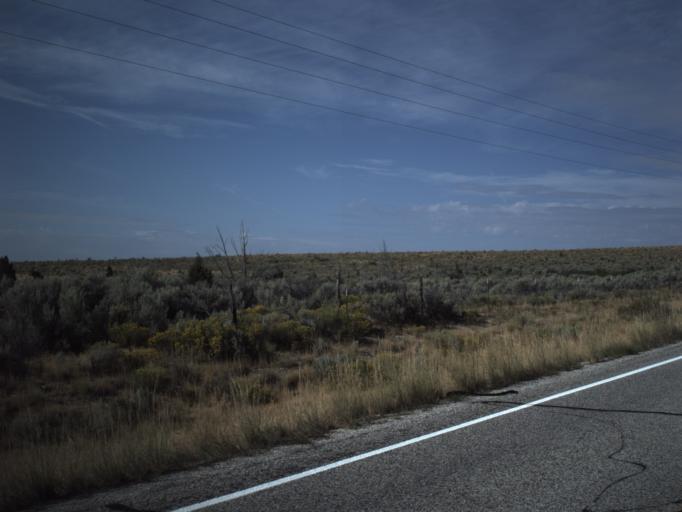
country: US
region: Idaho
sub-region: Cassia County
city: Burley
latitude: 41.8173
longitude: -113.2504
